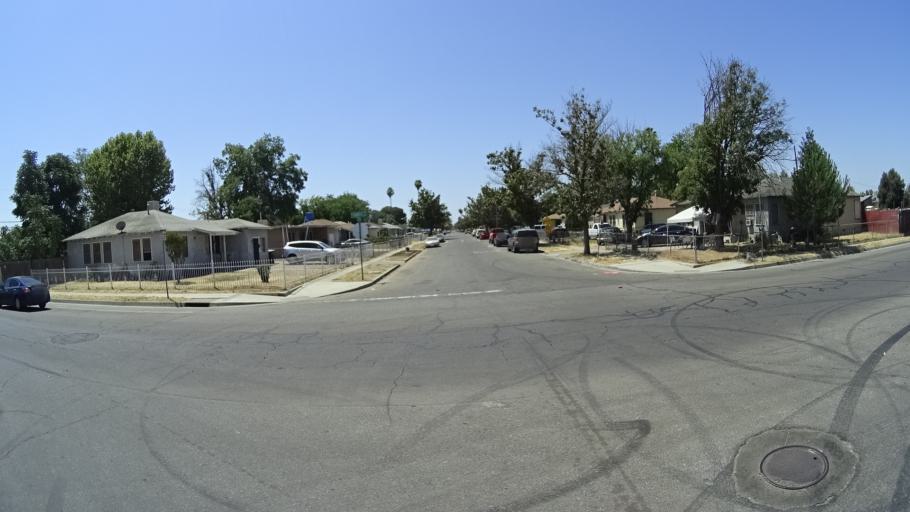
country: US
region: California
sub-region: Fresno County
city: Fresno
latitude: 36.7142
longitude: -119.7884
